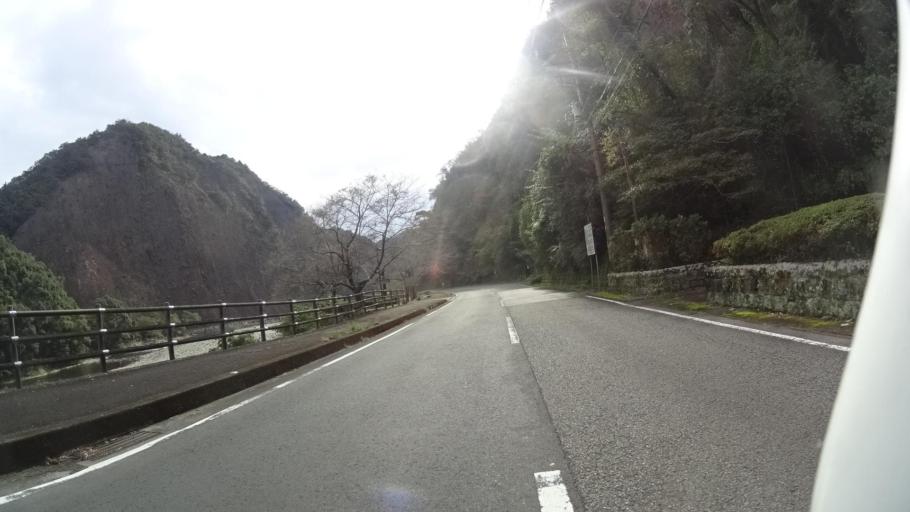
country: JP
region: Wakayama
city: Shingu
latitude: 33.5473
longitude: 135.7174
